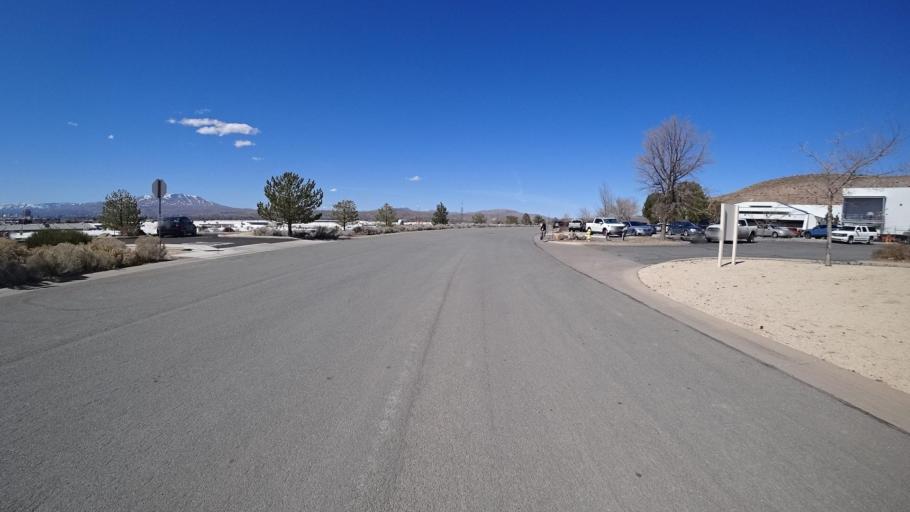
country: US
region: Nevada
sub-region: Washoe County
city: Sparks
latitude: 39.5328
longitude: -119.7015
